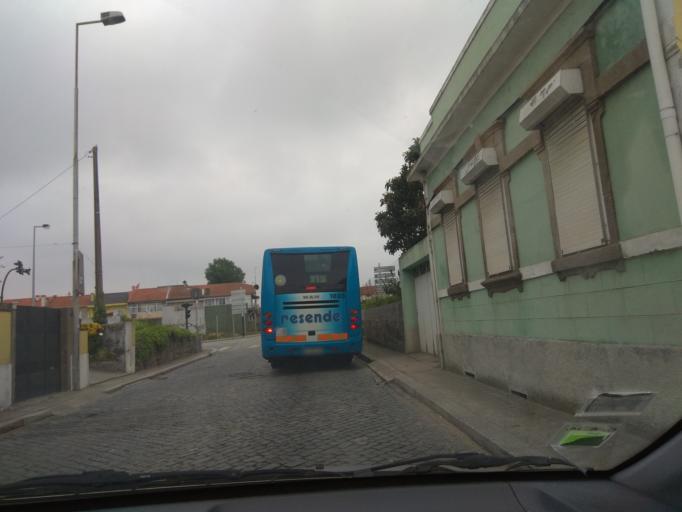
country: PT
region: Porto
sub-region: Matosinhos
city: Guifoes
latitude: 41.1950
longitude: -8.6618
